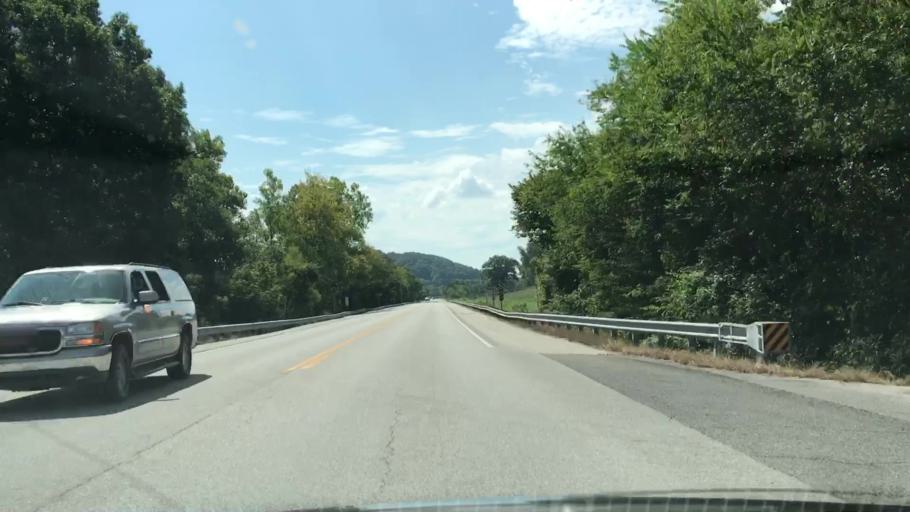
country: US
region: Tennessee
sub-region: Smith County
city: Carthage
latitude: 36.3150
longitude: -86.0099
